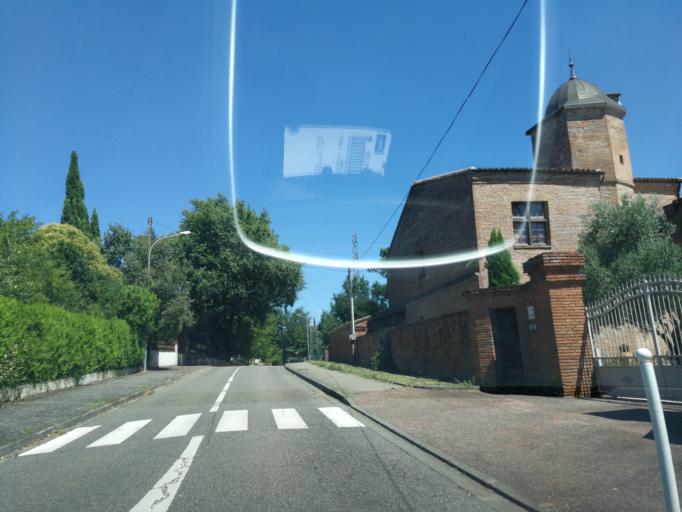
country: FR
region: Midi-Pyrenees
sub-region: Departement de la Haute-Garonne
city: Balma
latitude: 43.6131
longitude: 1.5071
